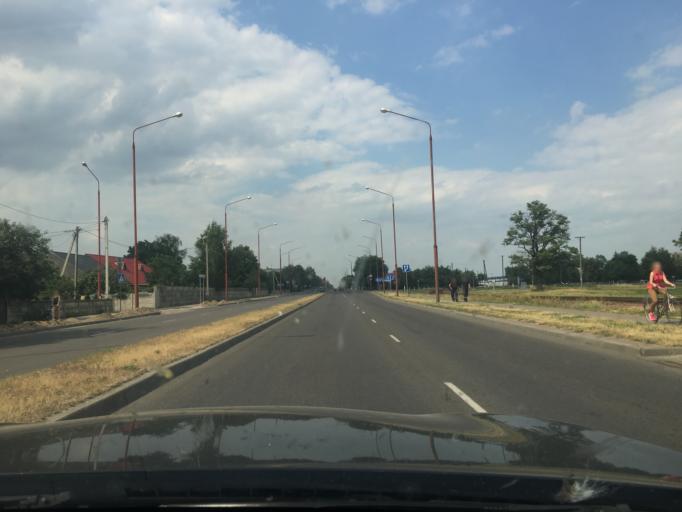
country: BY
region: Brest
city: Brest
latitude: 52.1134
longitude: 23.6686
